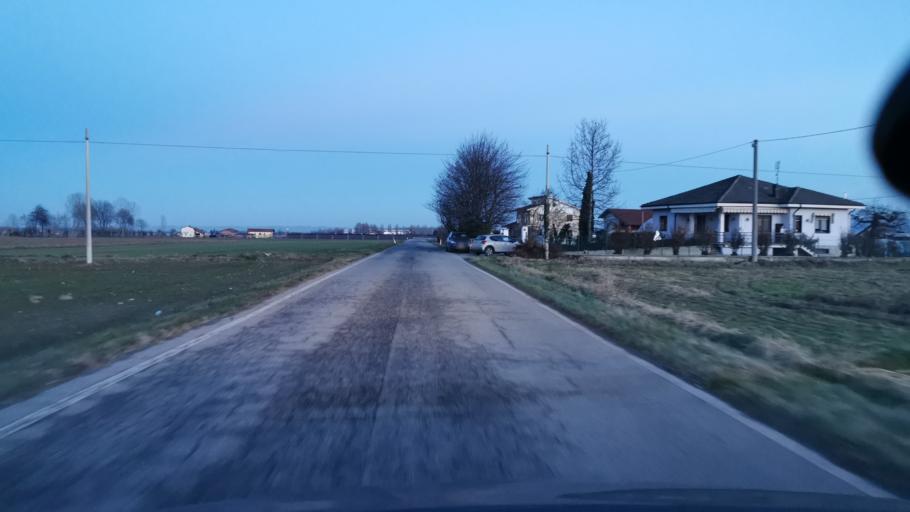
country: IT
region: Piedmont
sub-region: Provincia di Cuneo
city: Roata Rossi
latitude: 44.4579
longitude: 7.5095
